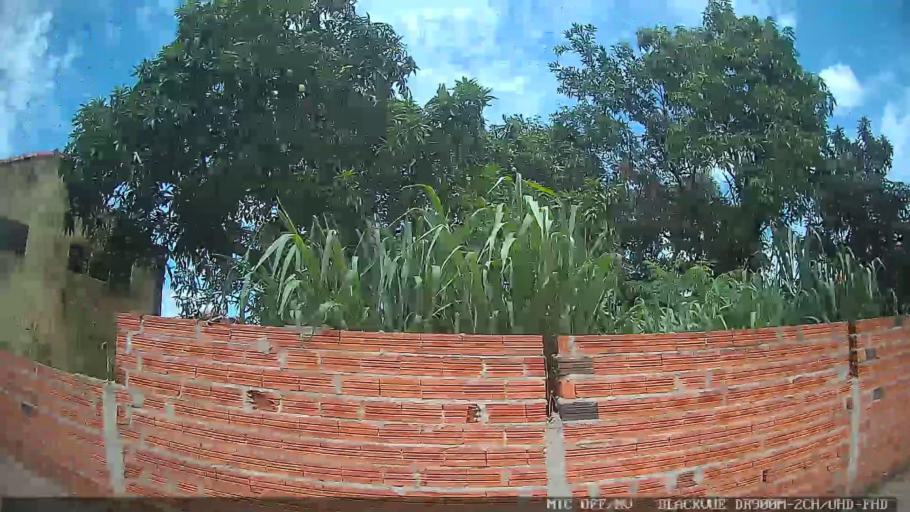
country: BR
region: Sao Paulo
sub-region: Laranjal Paulista
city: Laranjal Paulista
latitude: -23.0396
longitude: -47.8249
